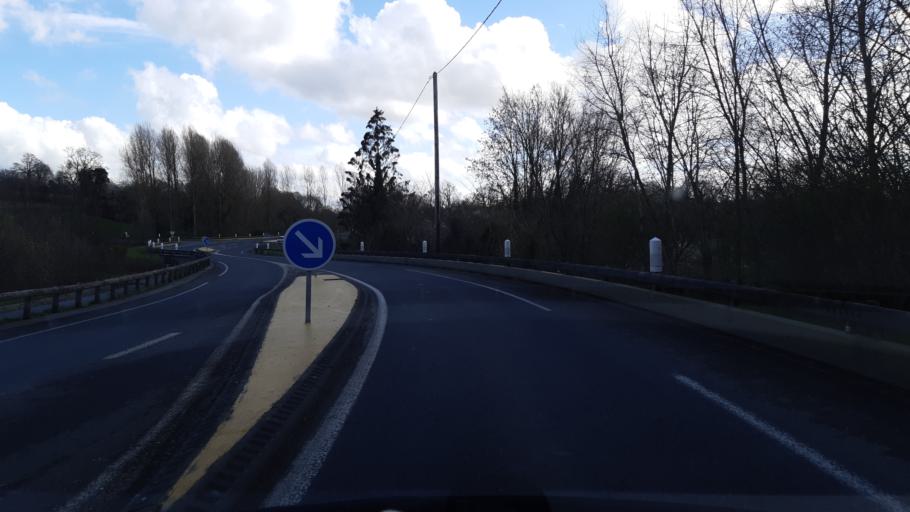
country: FR
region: Lower Normandy
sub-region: Departement de la Manche
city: Agneaux
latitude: 49.0708
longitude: -1.1305
